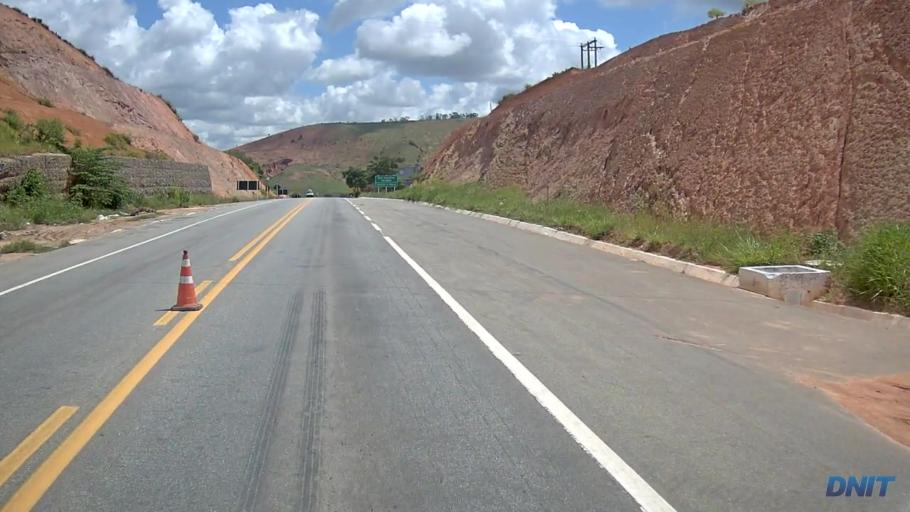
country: BR
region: Minas Gerais
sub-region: Governador Valadares
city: Governador Valadares
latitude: -18.8959
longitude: -42.0045
